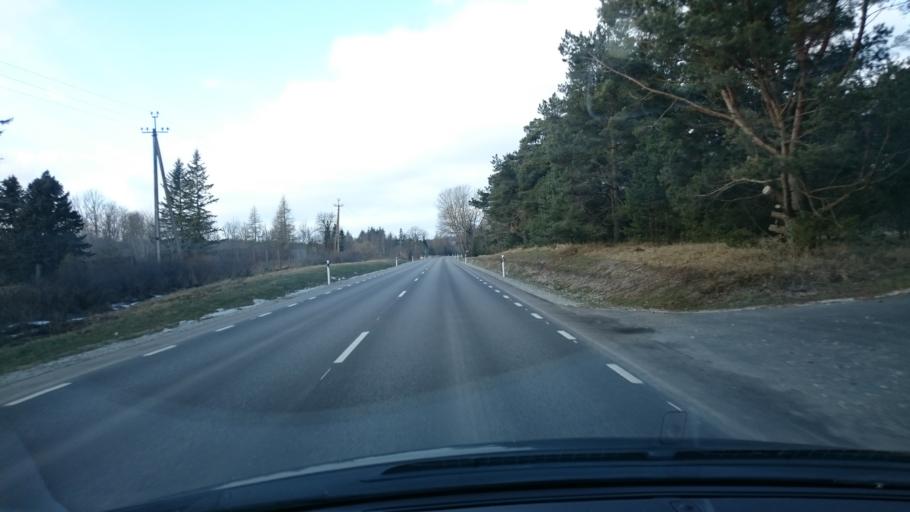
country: EE
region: Harju
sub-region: Keila linn
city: Keila
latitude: 59.3937
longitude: 24.2880
